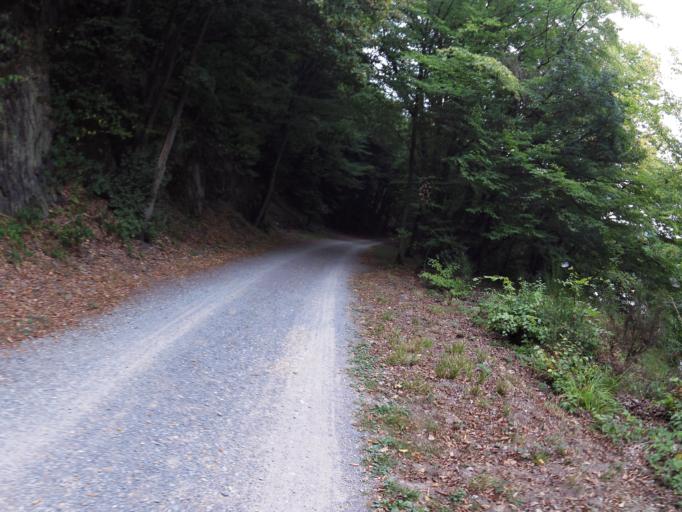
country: DE
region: North Rhine-Westphalia
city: Heimbach
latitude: 50.5990
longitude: 6.4478
